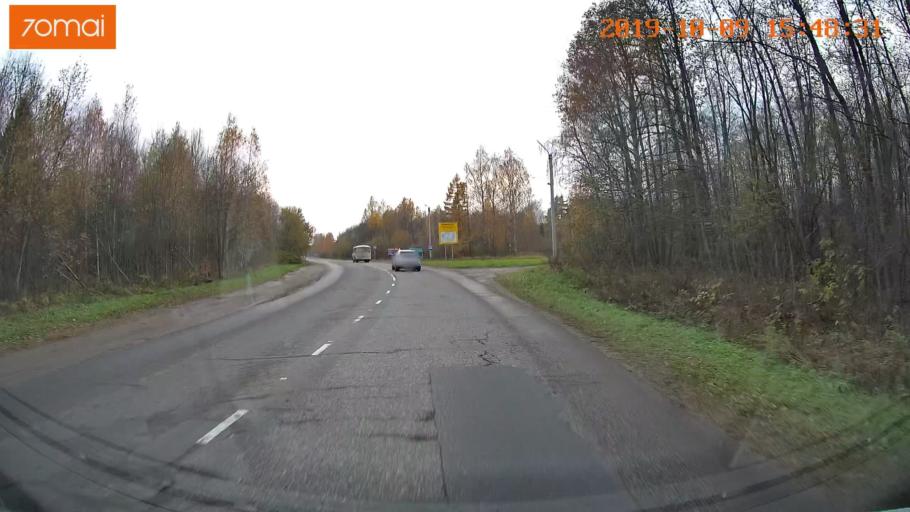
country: RU
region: Kostroma
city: Oktyabr'skiy
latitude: 57.8114
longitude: 41.0142
